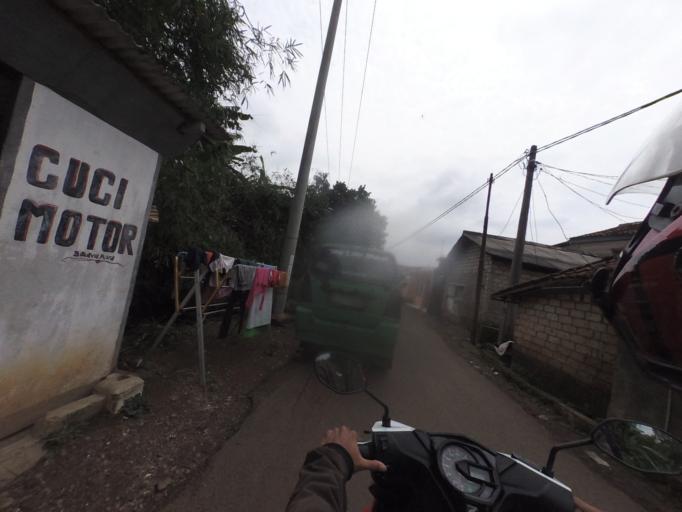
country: ID
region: West Java
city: Bogor
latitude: -6.6144
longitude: 106.7505
